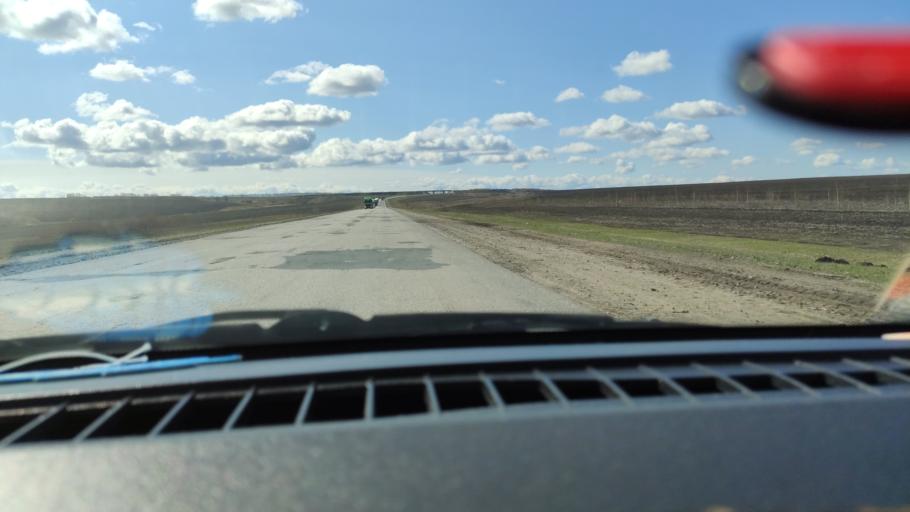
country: RU
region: Samara
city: Varlamovo
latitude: 53.0099
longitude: 48.3323
